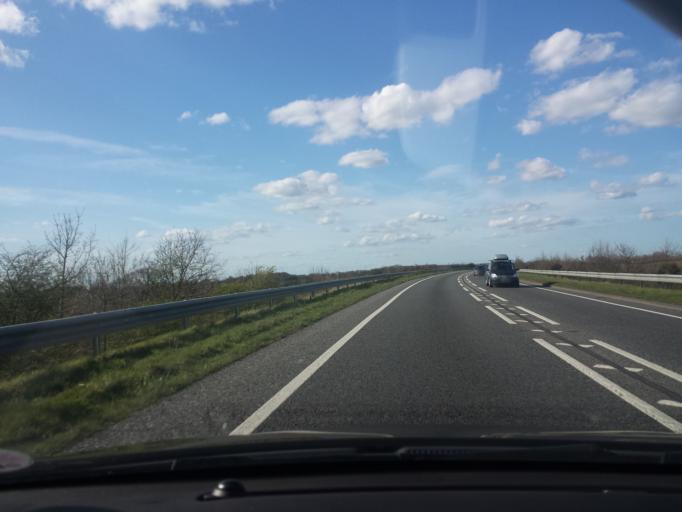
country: GB
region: England
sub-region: Essex
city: Great Bentley
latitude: 51.8491
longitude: 1.1028
